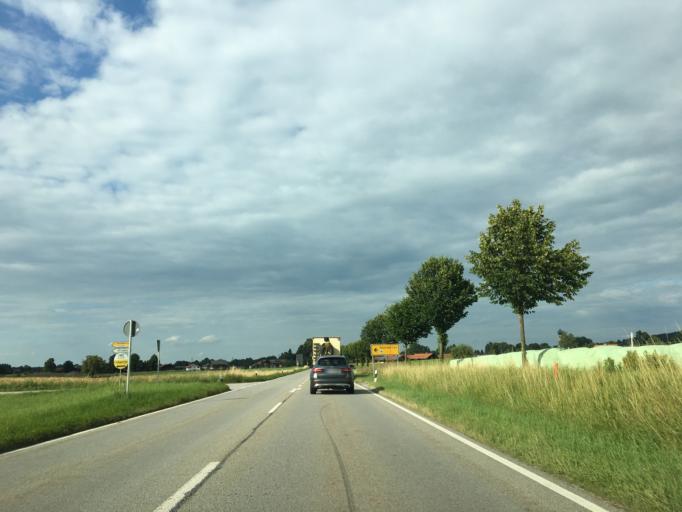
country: DE
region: Bavaria
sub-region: Upper Bavaria
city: Warngau
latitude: 47.8267
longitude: 11.7135
